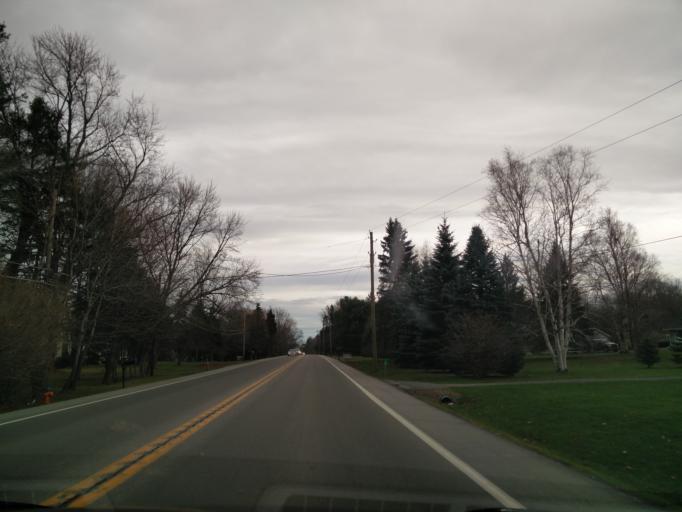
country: US
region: New York
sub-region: Tompkins County
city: Northwest Ithaca
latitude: 42.4789
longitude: -76.5595
